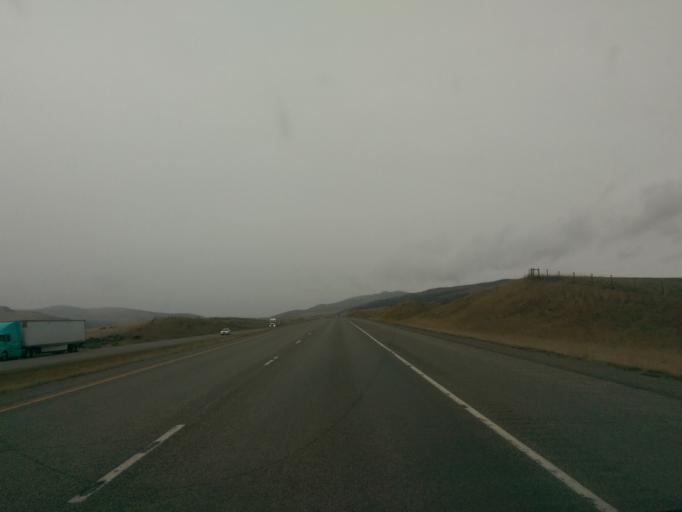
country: US
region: Montana
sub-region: Gallatin County
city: Three Forks
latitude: 45.9125
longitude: -111.7699
